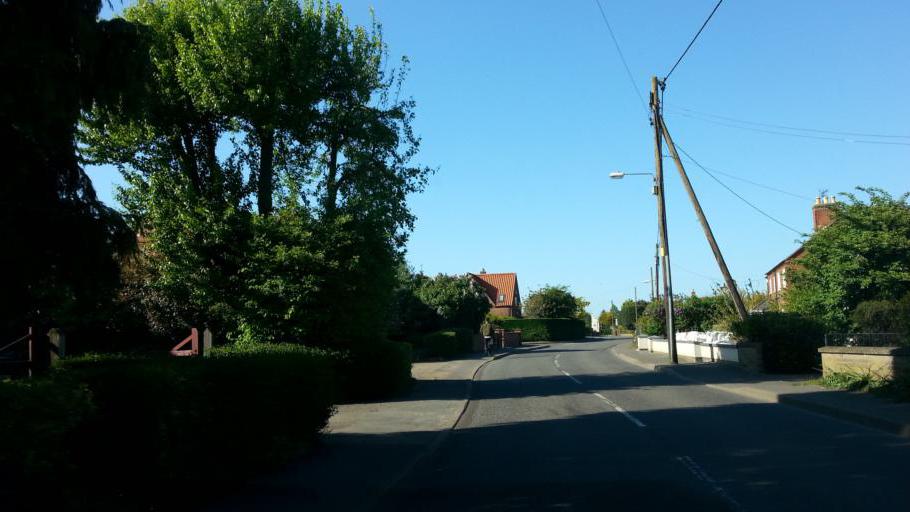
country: GB
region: England
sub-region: Lincolnshire
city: Great Gonerby
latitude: 52.9809
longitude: -0.6745
